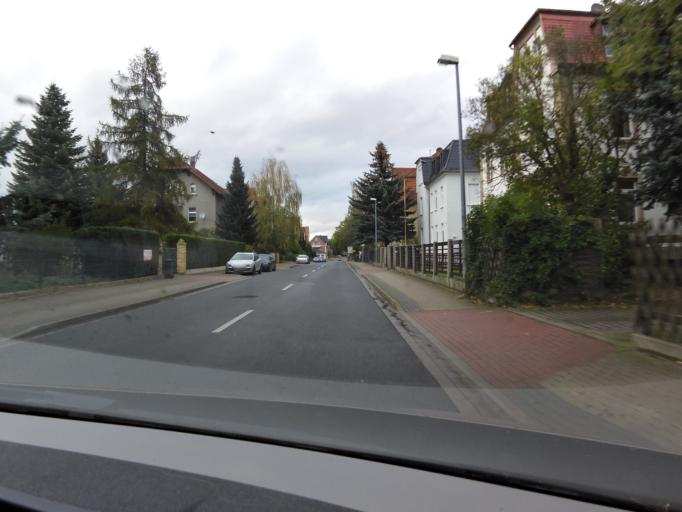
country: DE
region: Saxony
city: Bohlen
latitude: 51.2294
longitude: 12.3850
